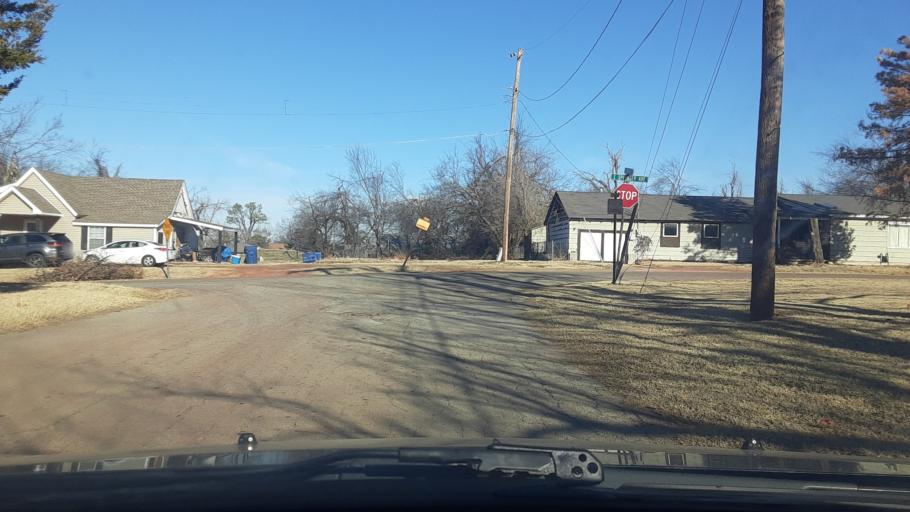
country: US
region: Oklahoma
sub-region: Logan County
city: Guthrie
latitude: 35.8756
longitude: -97.4040
